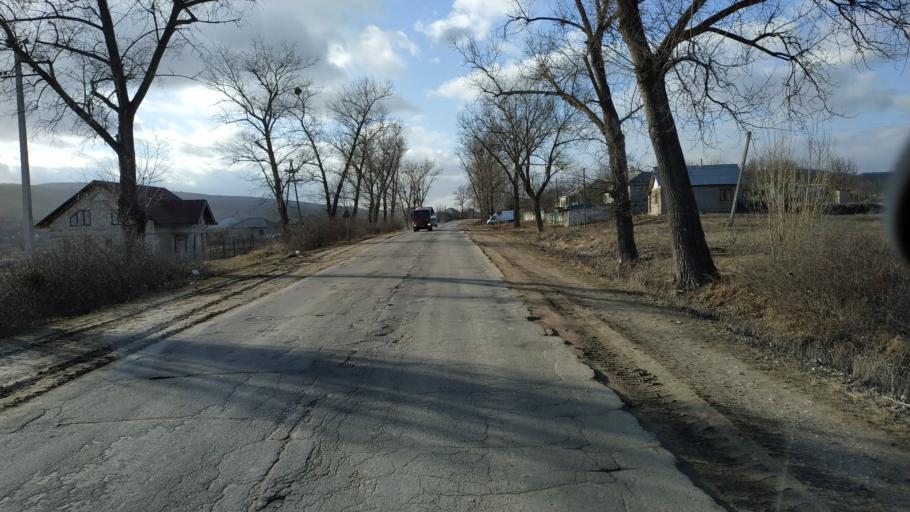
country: MD
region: Calarasi
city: Calarasi
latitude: 47.3282
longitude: 28.0948
